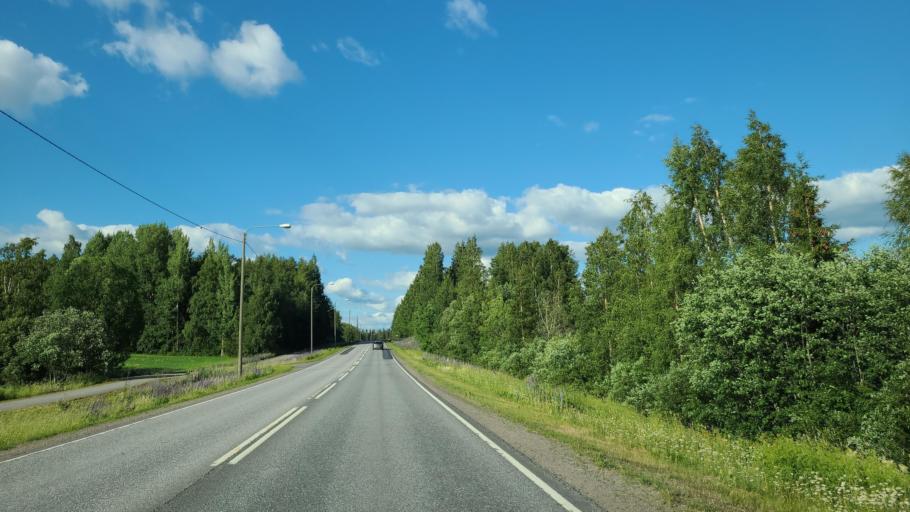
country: FI
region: Southern Ostrobothnia
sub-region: Kuusiokunnat
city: Toeysae
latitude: 62.6100
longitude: 23.7559
